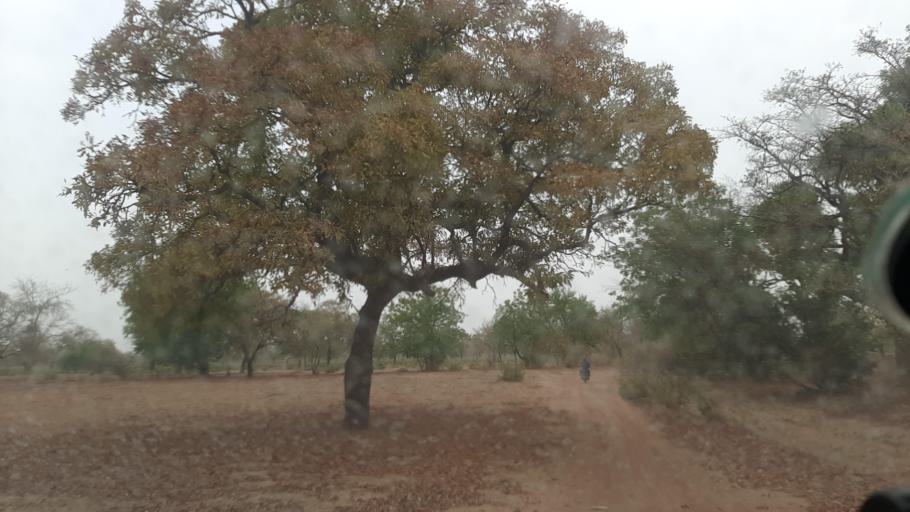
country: BF
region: Boucle du Mouhoun
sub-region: Province des Banwa
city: Salanso
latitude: 11.8496
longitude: -4.4236
